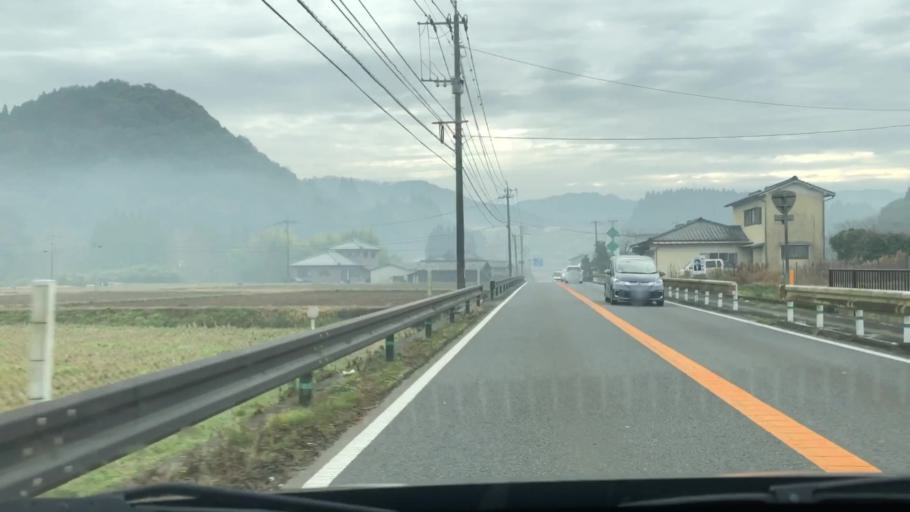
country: JP
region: Oita
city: Usuki
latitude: 33.0192
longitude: 131.6990
